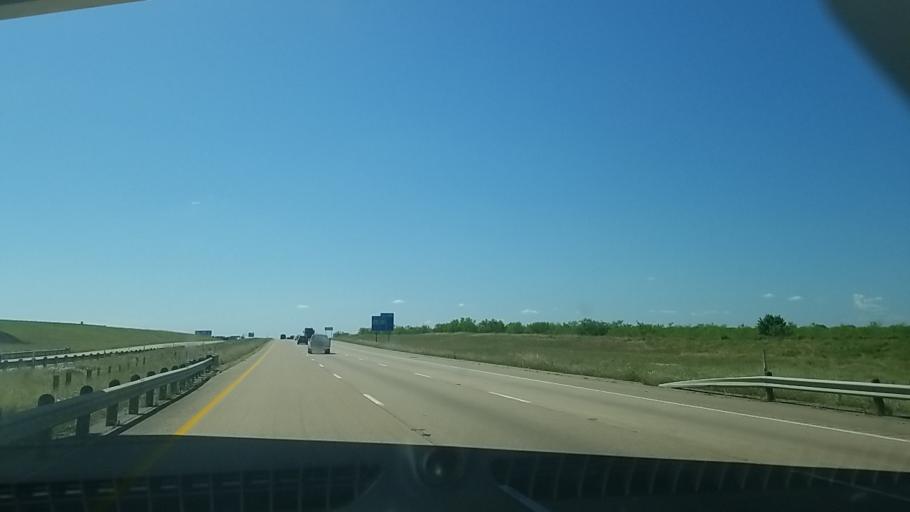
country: US
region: Texas
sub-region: Ellis County
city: Ennis
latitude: 32.2979
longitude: -96.5695
